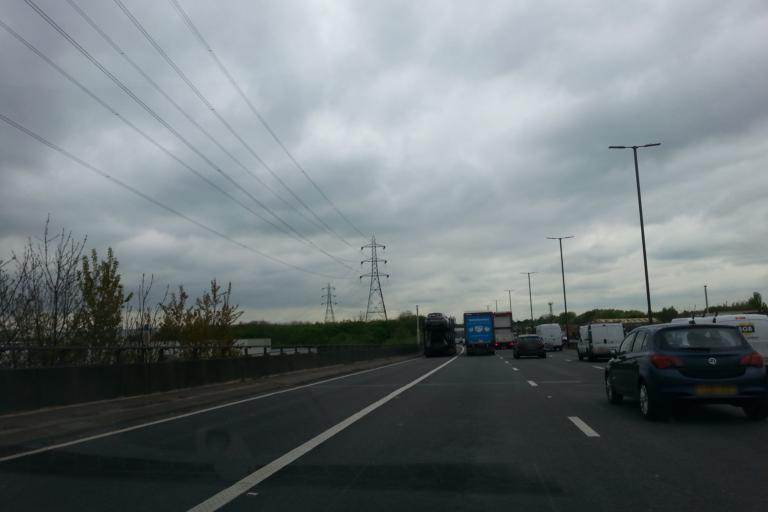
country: GB
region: England
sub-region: City and Borough of Birmingham
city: Hockley
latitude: 52.5229
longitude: -1.8818
